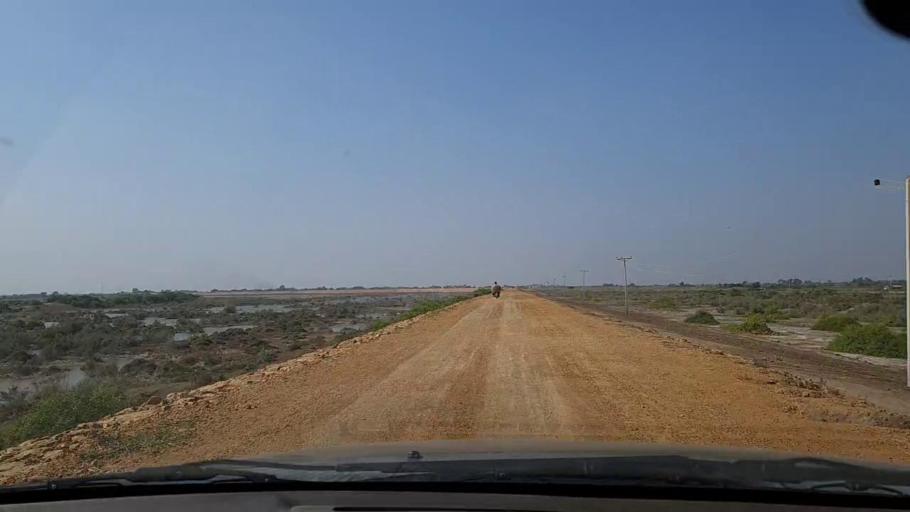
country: PK
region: Sindh
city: Chuhar Jamali
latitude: 24.4558
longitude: 67.8736
